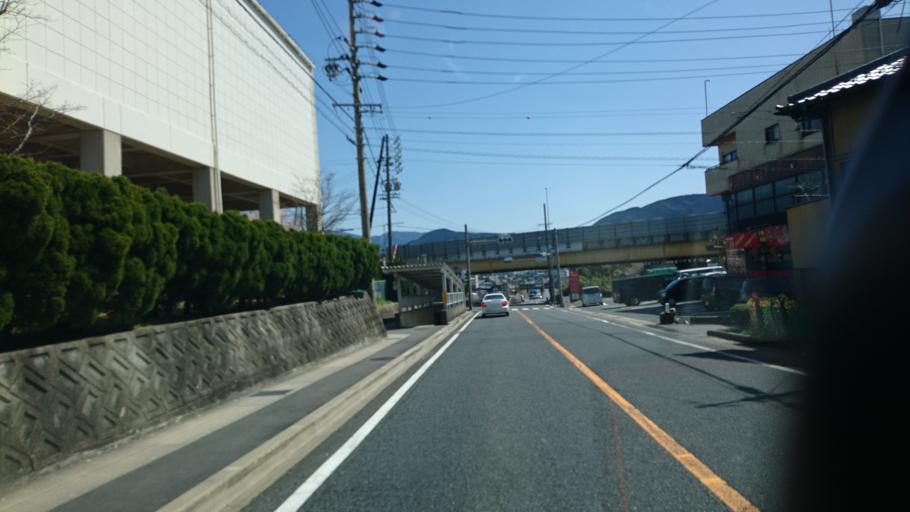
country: JP
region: Gifu
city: Nakatsugawa
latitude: 35.4555
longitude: 137.3963
